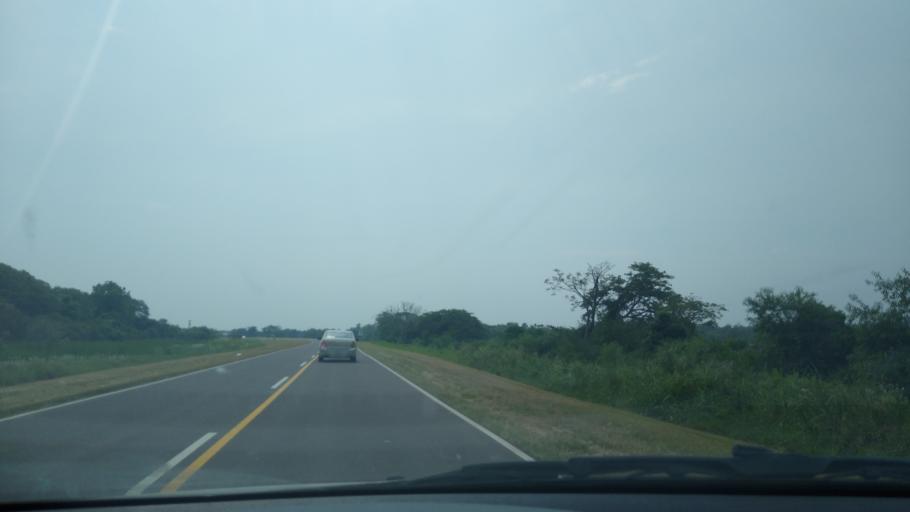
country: AR
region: Chaco
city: La Eduvigis
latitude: -26.8435
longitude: -59.0530
